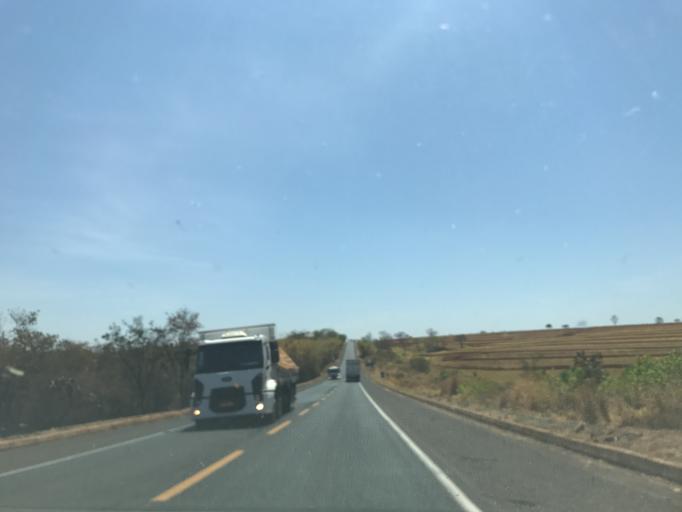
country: BR
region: Minas Gerais
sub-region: Prata
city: Prata
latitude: -19.5076
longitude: -48.8459
